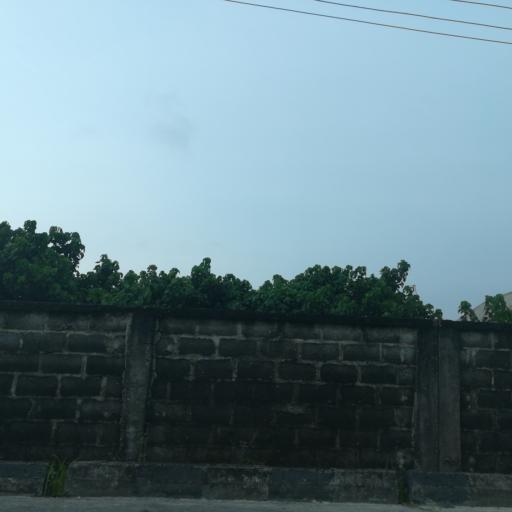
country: NG
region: Rivers
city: Port Harcourt
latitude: 4.7494
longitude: 7.0050
